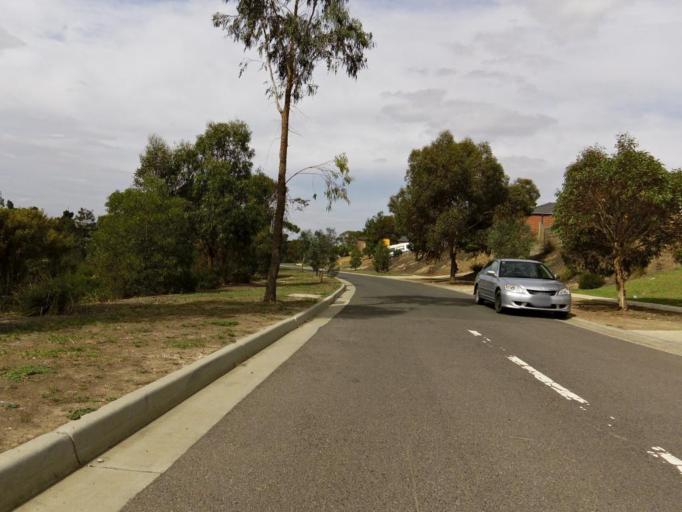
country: AU
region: Victoria
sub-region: Hume
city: Sunbury
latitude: -37.5633
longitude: 144.7002
